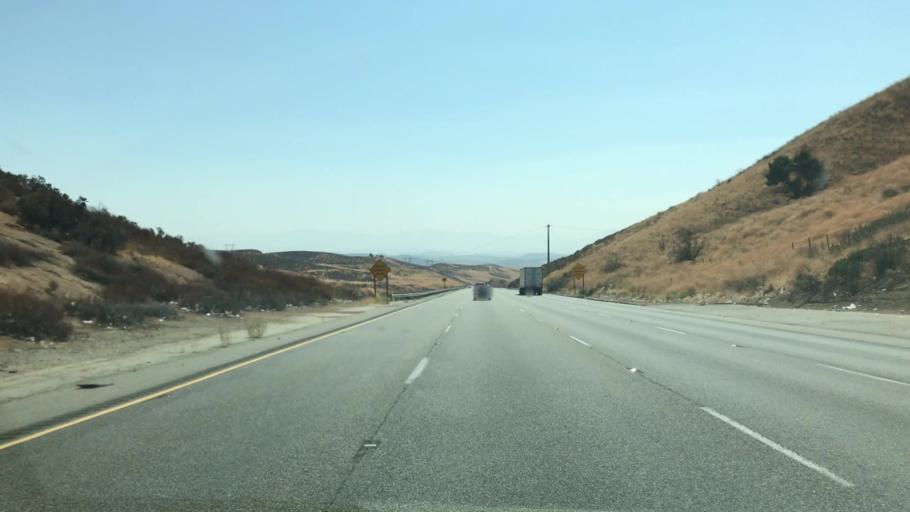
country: US
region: California
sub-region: Los Angeles County
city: Castaic
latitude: 34.5518
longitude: -118.6677
